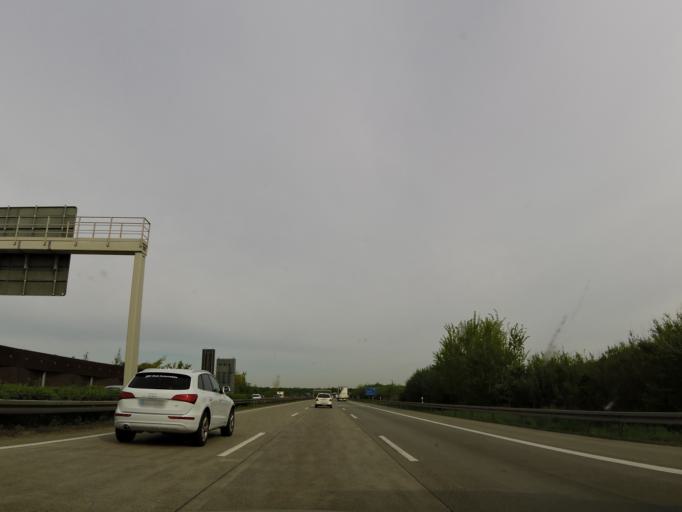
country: DE
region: Lower Saxony
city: Isernhagen Farster Bauerschaft
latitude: 52.4404
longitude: 9.8726
